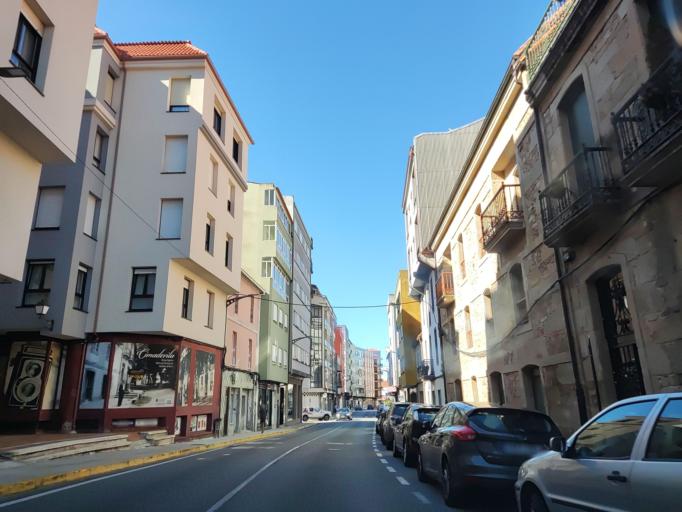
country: ES
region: Galicia
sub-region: Provincia da Coruna
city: Boiro
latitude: 42.6491
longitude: -8.8805
